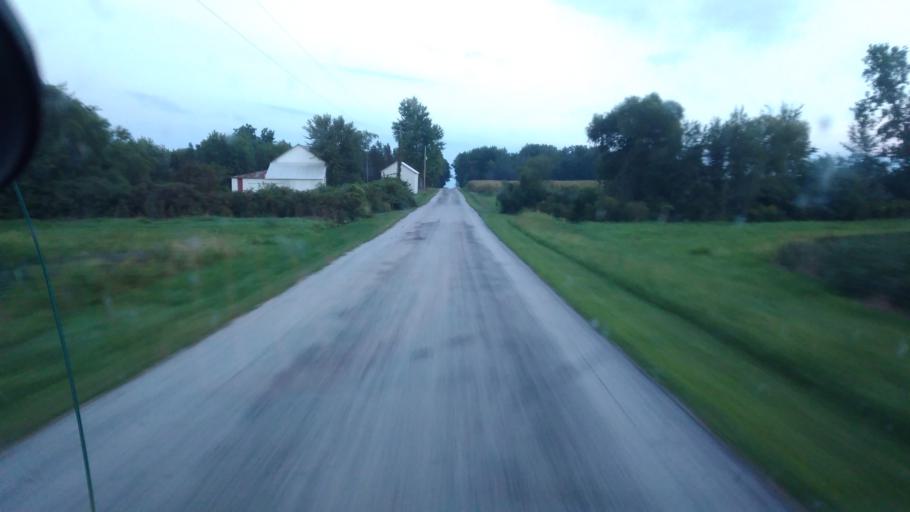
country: US
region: Ohio
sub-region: Hardin County
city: Kenton
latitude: 40.6570
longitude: -83.4589
